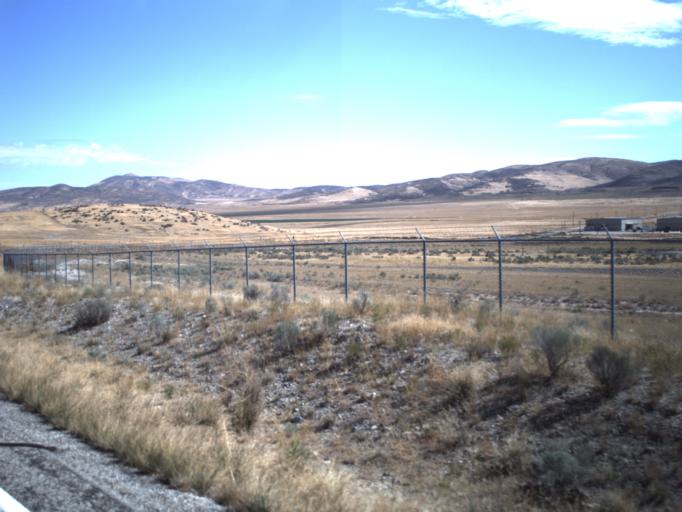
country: US
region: Utah
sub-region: Box Elder County
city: Tremonton
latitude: 41.7205
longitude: -112.4506
